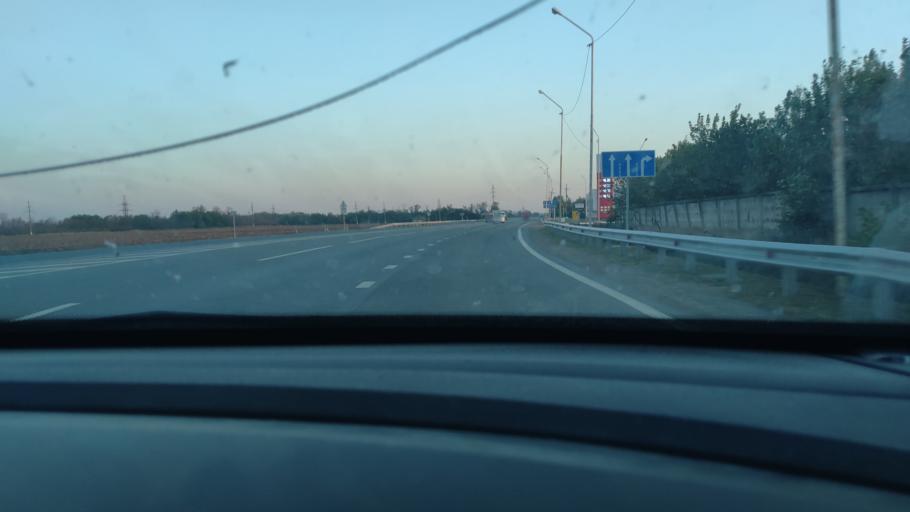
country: RU
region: Krasnodarskiy
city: Timashevsk
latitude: 45.6245
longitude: 38.9859
